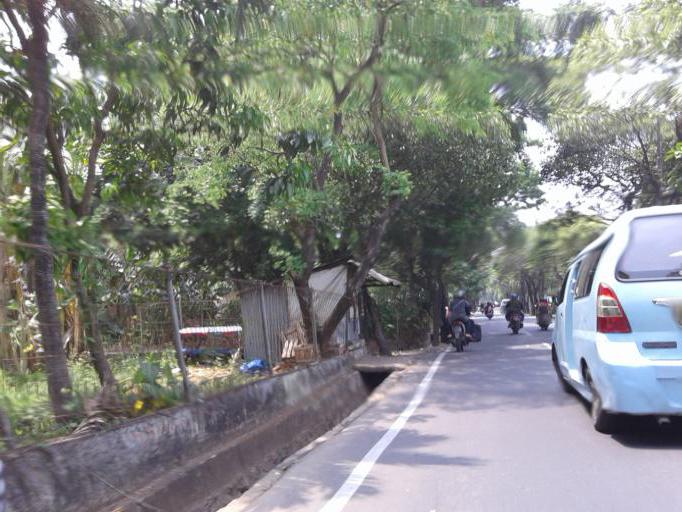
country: ID
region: West Java
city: Pamulang
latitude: -6.3116
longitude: 106.8163
